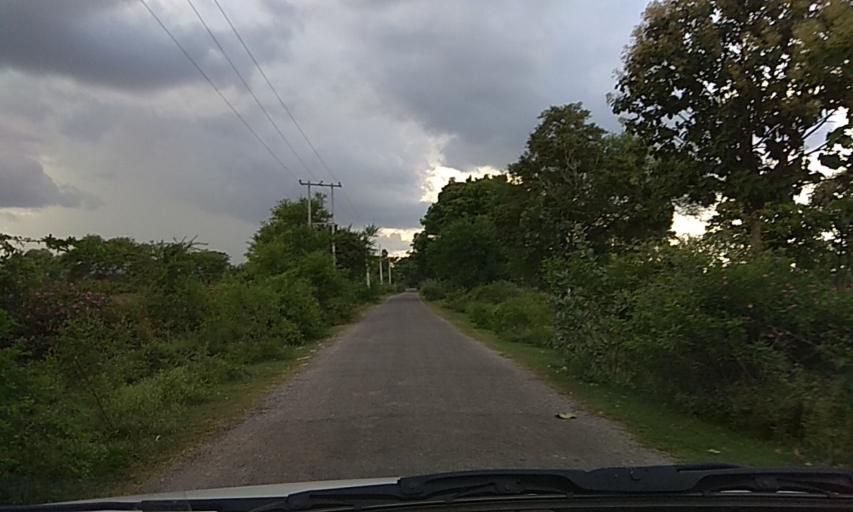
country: IN
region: Karnataka
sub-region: Chamrajnagar
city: Gundlupet
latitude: 11.8715
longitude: 76.7423
